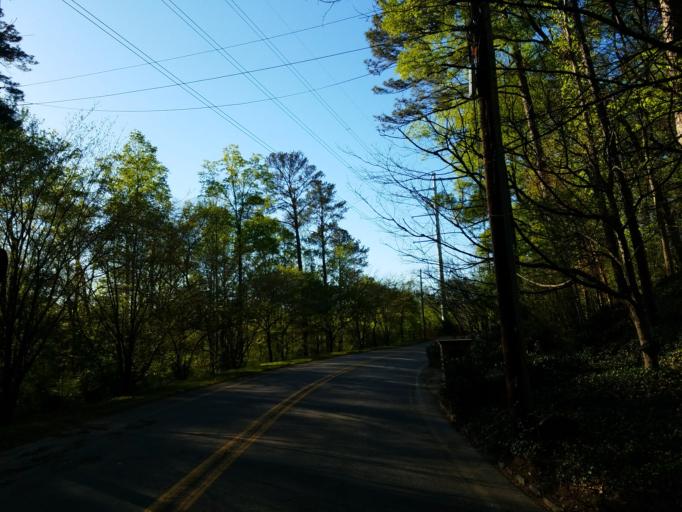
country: US
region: Georgia
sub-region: Cobb County
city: Vinings
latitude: 33.8420
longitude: -84.4582
